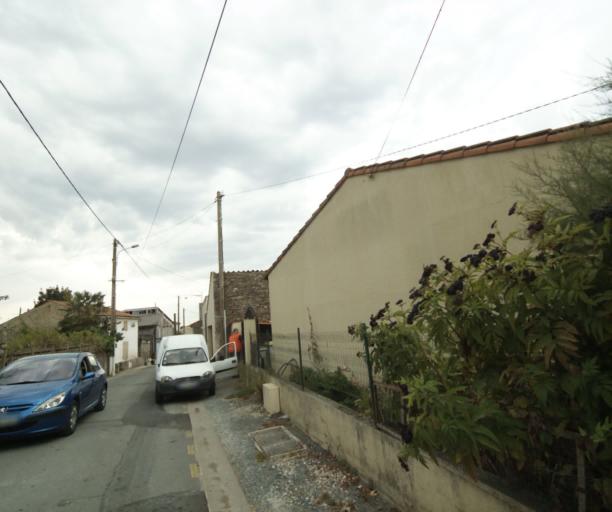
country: FR
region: Poitou-Charentes
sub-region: Departement de la Charente-Maritime
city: Tonnay-Charente
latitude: 45.9498
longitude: -0.8786
